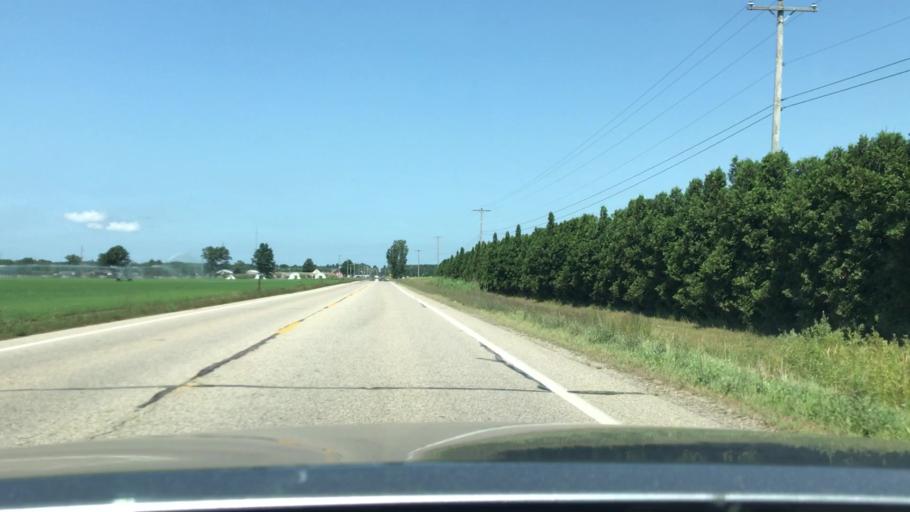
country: US
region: Michigan
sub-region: Ottawa County
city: Allendale
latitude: 42.9650
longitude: -86.0828
